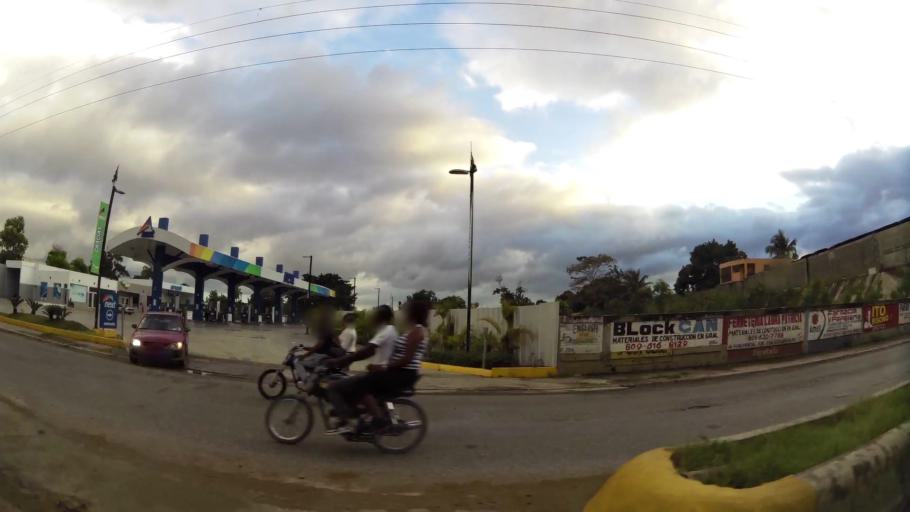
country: DO
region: Nacional
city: Santo Domingo
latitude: 18.5075
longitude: -69.9917
